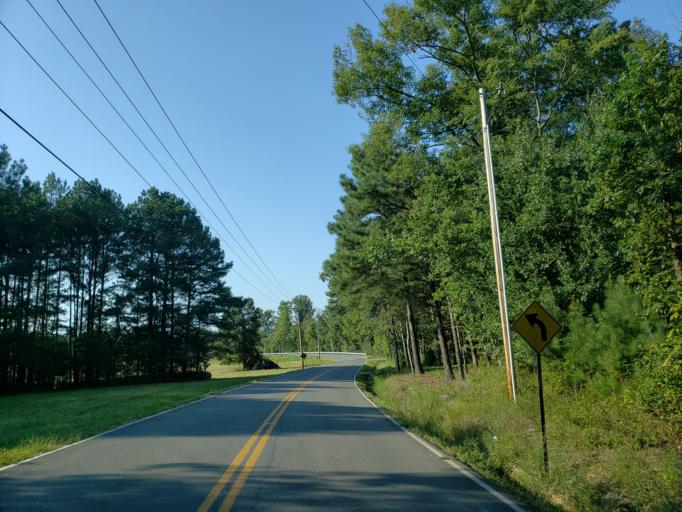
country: US
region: Tennessee
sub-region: Bradley County
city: Wildwood Lake
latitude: 35.0446
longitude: -84.7457
